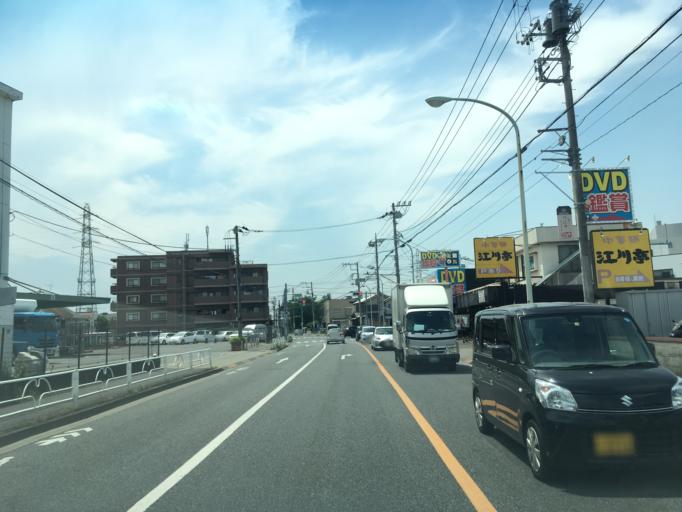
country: JP
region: Tokyo
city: Higashimurayama-shi
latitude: 35.7723
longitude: 139.4787
